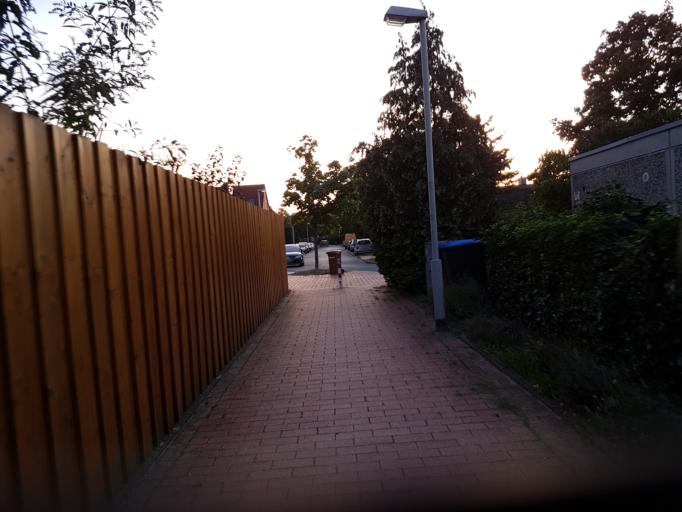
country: DE
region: Lower Saxony
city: Langenhagen
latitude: 52.4155
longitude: 9.7668
